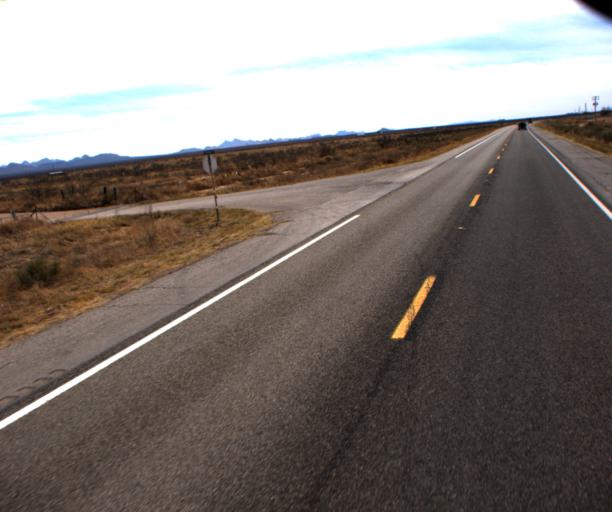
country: US
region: Arizona
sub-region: Cochise County
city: Pirtleville
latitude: 31.6565
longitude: -109.6761
